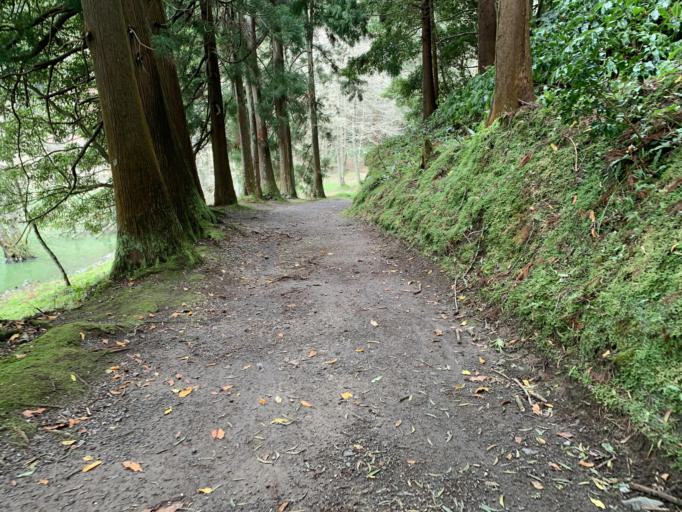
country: PT
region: Azores
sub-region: Povoacao
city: Furnas
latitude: 37.7641
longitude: -25.3347
